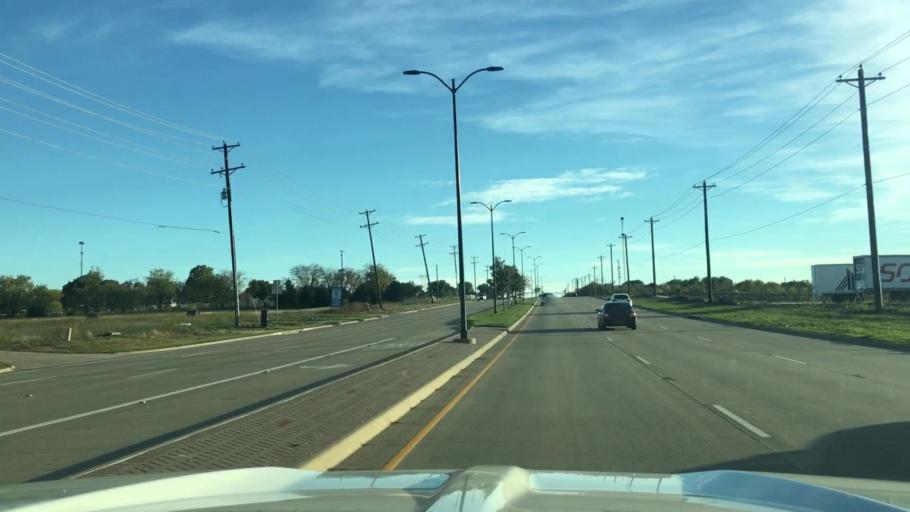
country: US
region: Texas
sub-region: Collin County
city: Prosper
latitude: 33.2111
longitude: -96.8027
